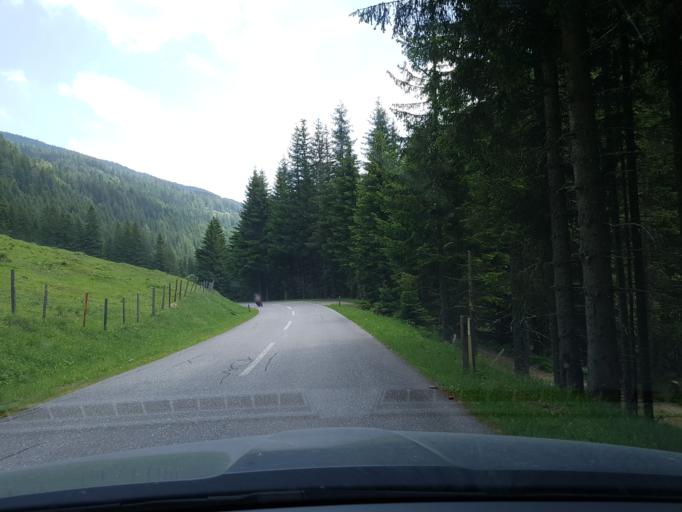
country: AT
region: Carinthia
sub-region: Politischer Bezirk Spittal an der Drau
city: Kleinkirchheim
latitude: 46.8909
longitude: 13.8329
